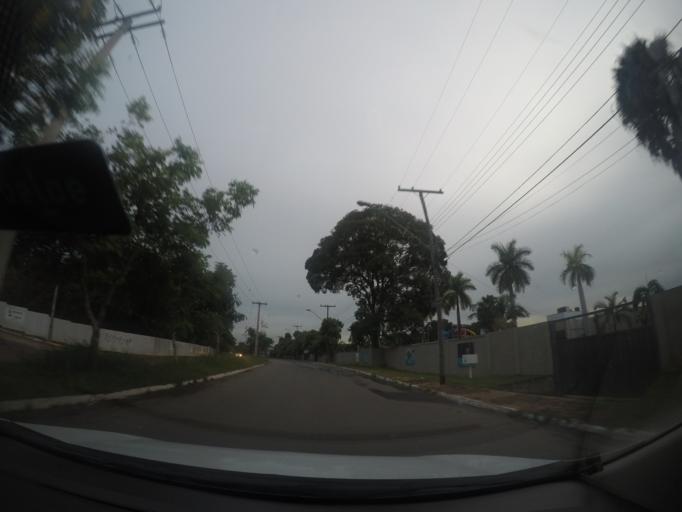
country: BR
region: Goias
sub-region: Goiania
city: Goiania
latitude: -16.6407
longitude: -49.2468
